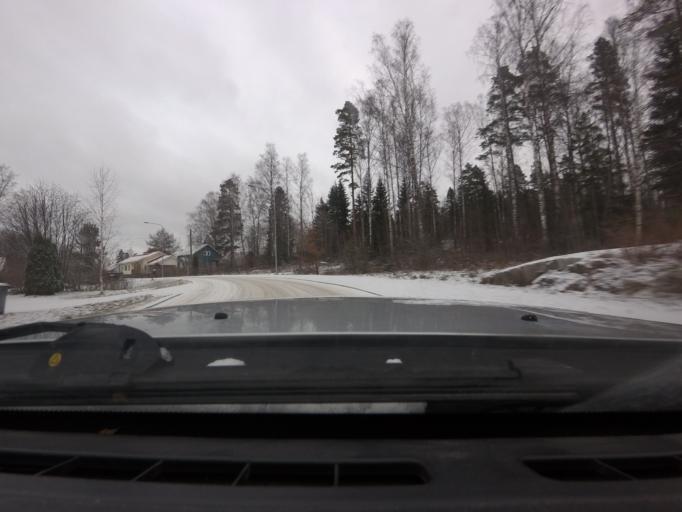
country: FI
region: Uusimaa
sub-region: Helsinki
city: Kilo
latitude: 60.2104
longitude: 24.7874
